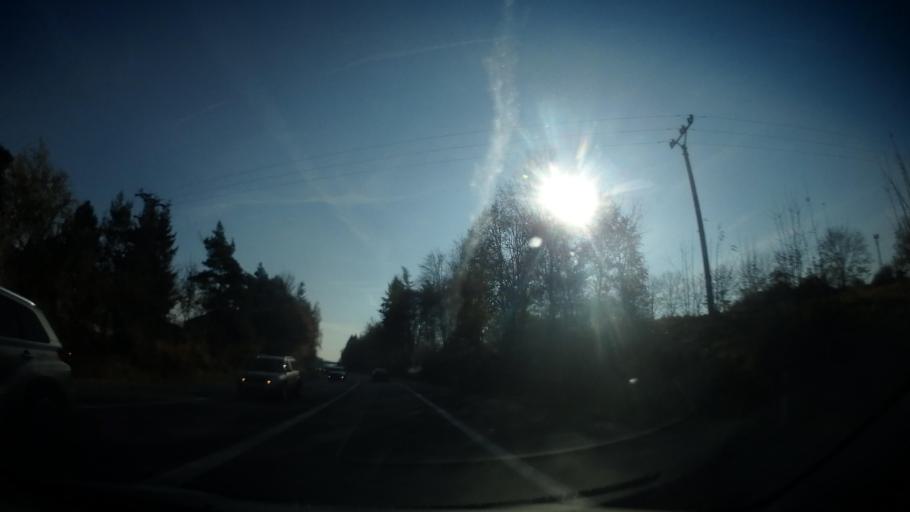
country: CZ
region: Central Bohemia
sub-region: Okres Praha-Vychod
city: Mnichovice
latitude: 49.8987
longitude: 14.7134
